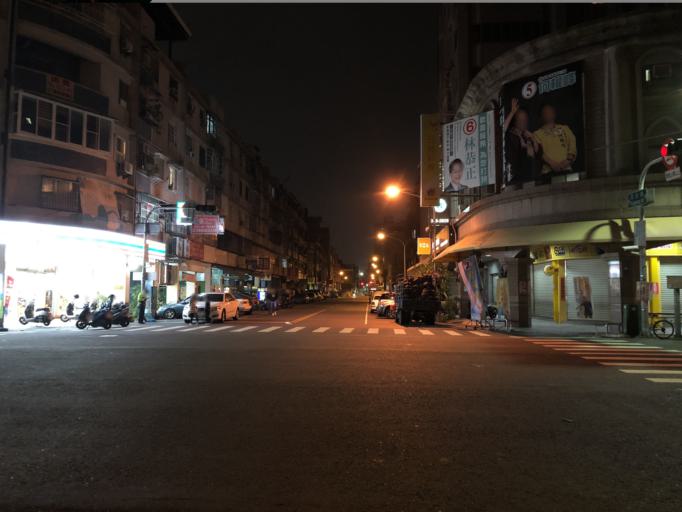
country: TW
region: Kaohsiung
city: Kaohsiung
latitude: 22.6374
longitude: 120.3320
